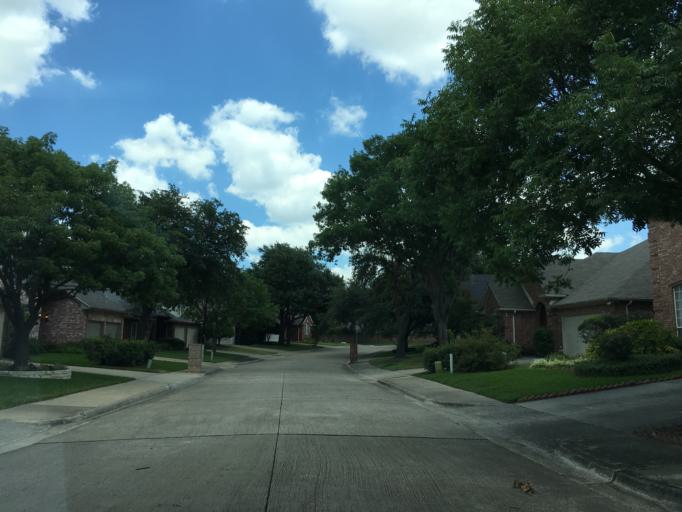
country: US
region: Texas
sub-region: Dallas County
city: Addison
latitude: 32.9465
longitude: -96.8504
